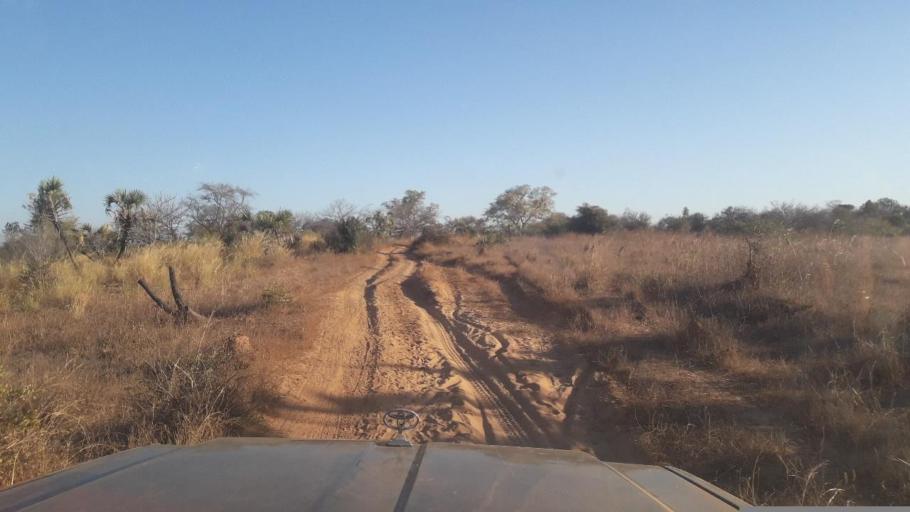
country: MG
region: Boeny
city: Sitampiky
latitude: -16.5003
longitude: 45.6033
